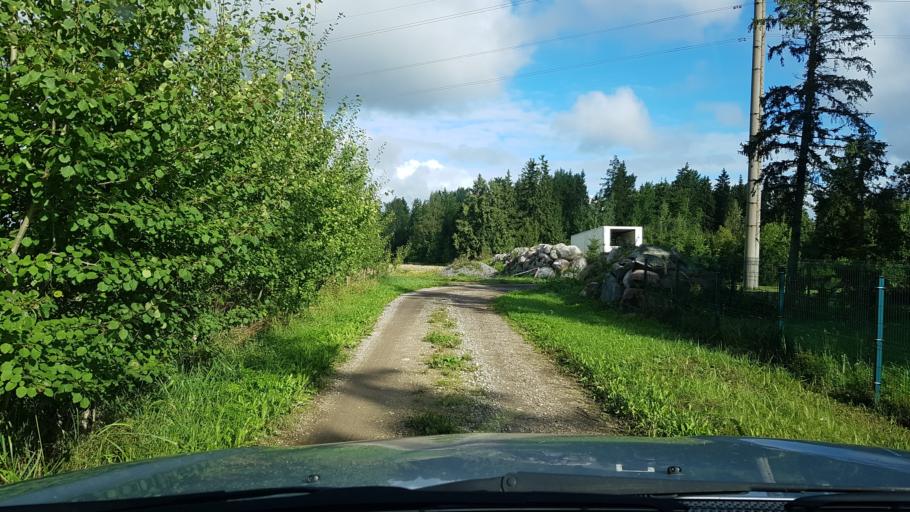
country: EE
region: Harju
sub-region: Rae vald
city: Vaida
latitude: 59.2680
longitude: 25.0226
